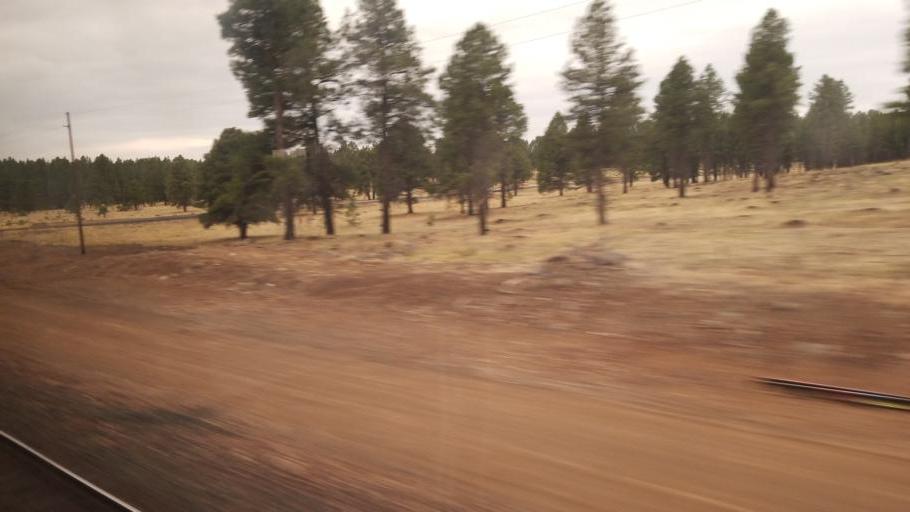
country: US
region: Arizona
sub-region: Coconino County
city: Parks
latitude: 35.2366
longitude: -112.0268
